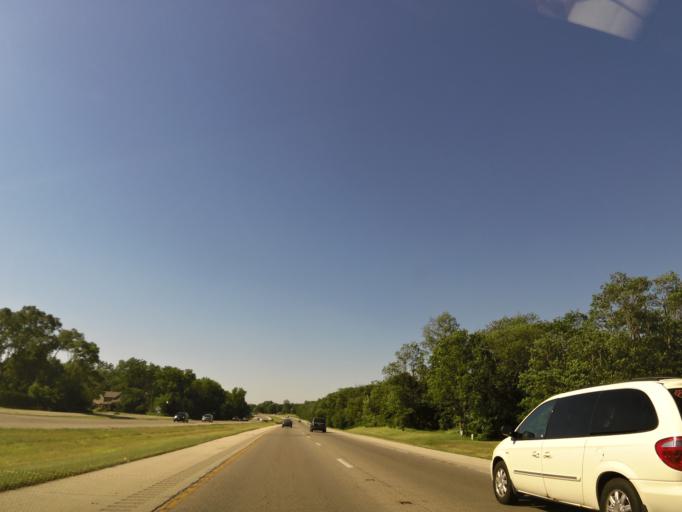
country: US
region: Illinois
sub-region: Winnebago County
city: Roscoe
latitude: 42.4141
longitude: -89.0131
